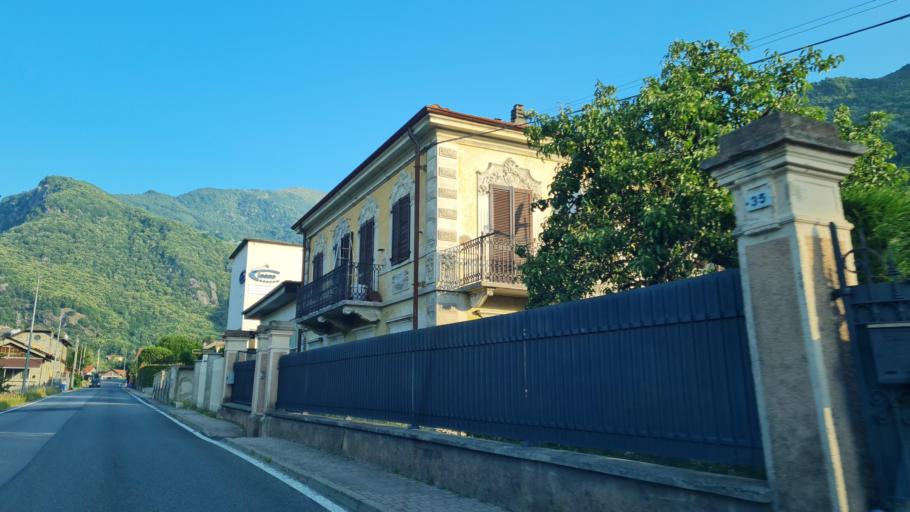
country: IT
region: Piedmont
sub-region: Provincia di Torino
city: Pont-Canavese
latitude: 45.4207
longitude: 7.6047
